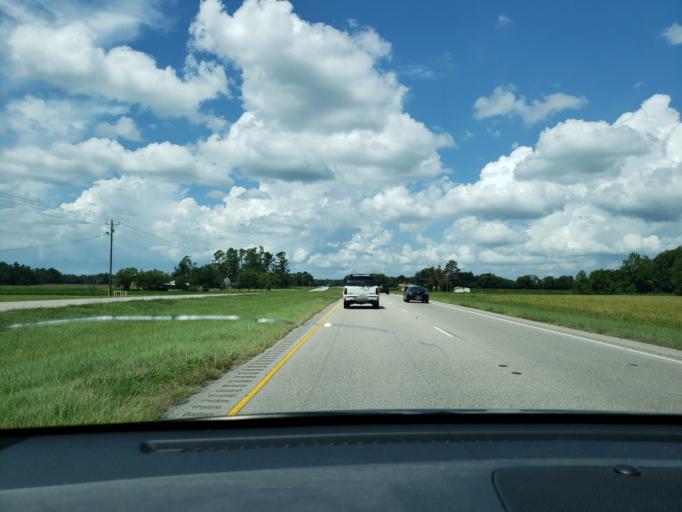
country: US
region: North Carolina
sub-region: Bladen County
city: Elizabethtown
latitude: 34.7110
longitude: -78.7465
